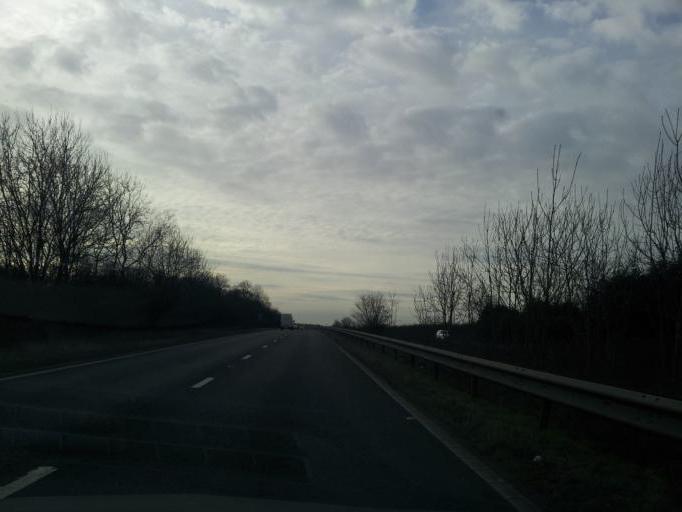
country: GB
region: England
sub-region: District of Rutland
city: Clipsham
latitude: 52.7234
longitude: -0.5961
